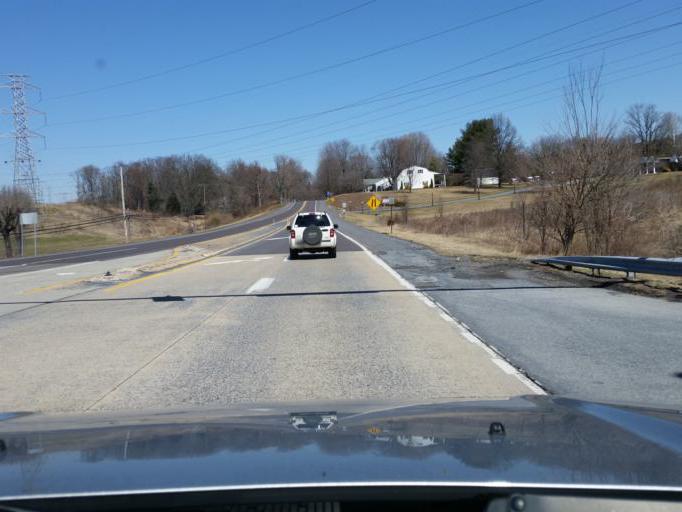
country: US
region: Pennsylvania
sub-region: Dauphin County
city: Middletown
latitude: 40.2300
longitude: -76.7184
